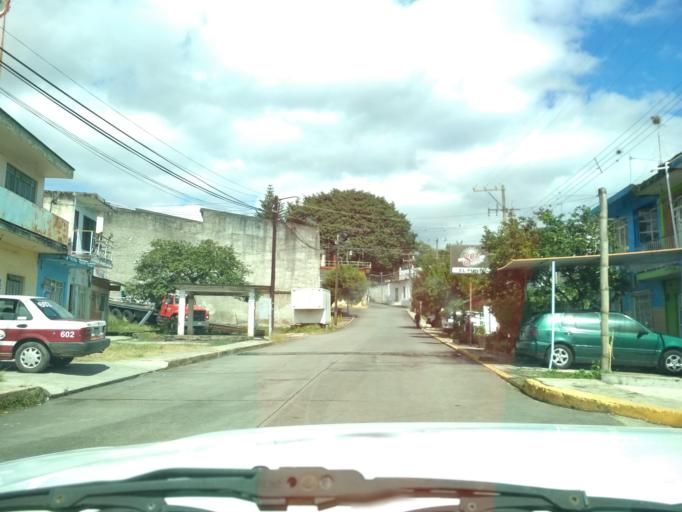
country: MX
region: Veracruz
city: Coatepec
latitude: 19.4511
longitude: -96.9368
